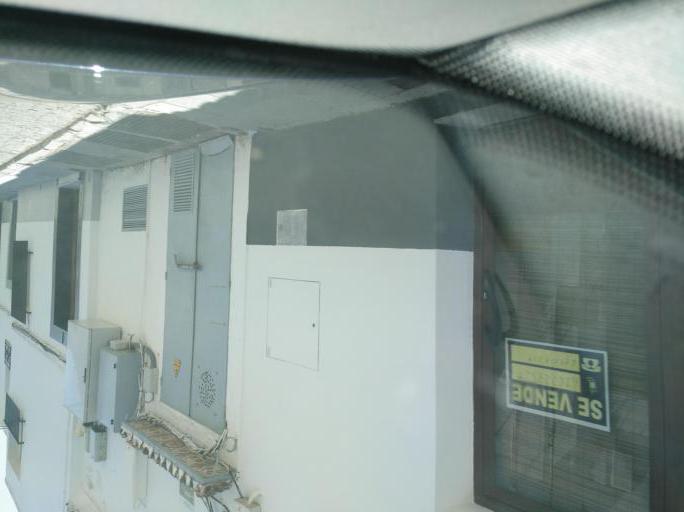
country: ES
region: Extremadura
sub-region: Provincia de Badajoz
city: Olivenza
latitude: 38.6846
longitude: -7.0991
